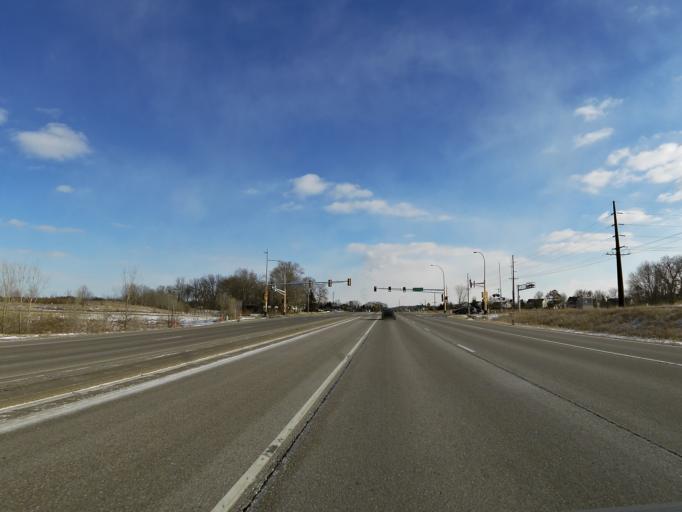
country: US
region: Minnesota
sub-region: Dakota County
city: Eagan
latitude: 44.8207
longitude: -93.1067
